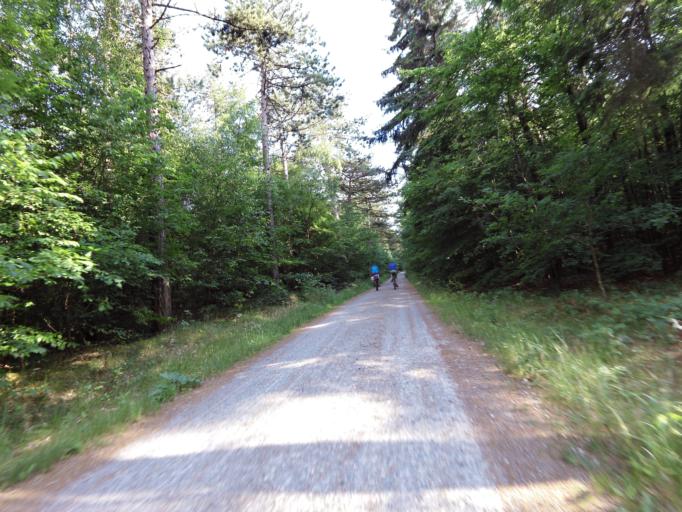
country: DE
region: Lower Saxony
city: Nordholz
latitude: 53.8564
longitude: 8.6015
